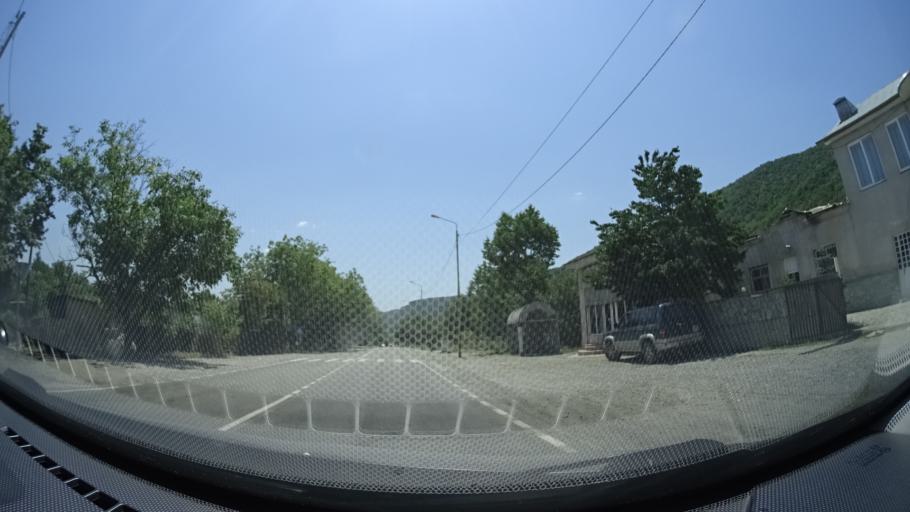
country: GE
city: Zhinvali
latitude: 42.0749
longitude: 44.7510
